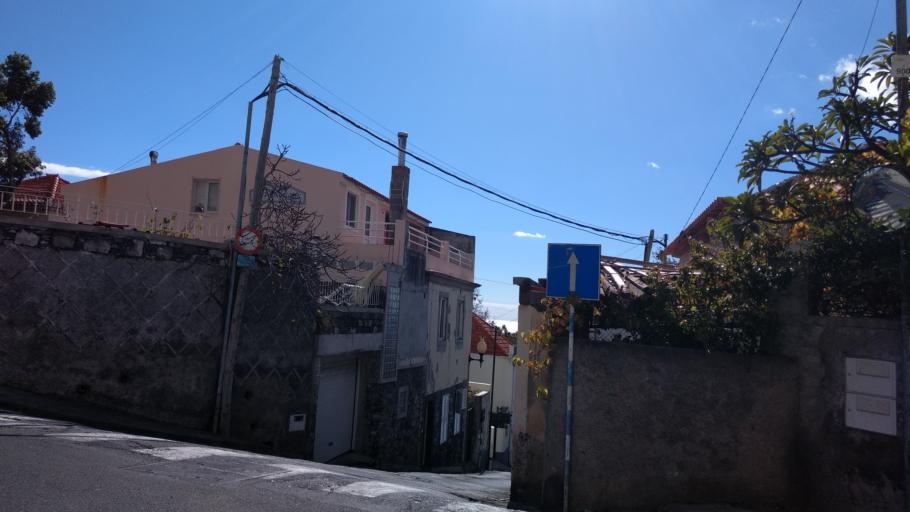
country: PT
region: Madeira
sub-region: Funchal
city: Nossa Senhora do Monte
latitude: 32.6572
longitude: -16.9075
